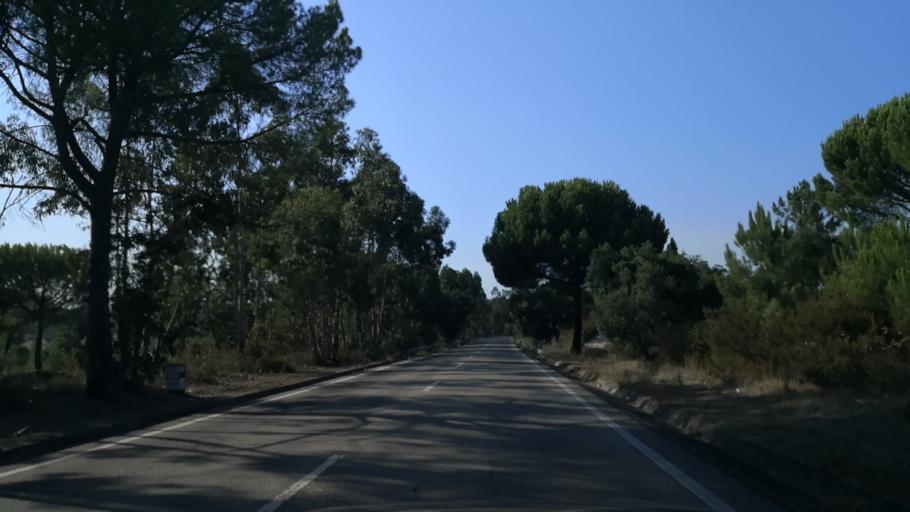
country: PT
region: Santarem
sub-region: Coruche
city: Coruche
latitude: 38.9860
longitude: -8.5501
